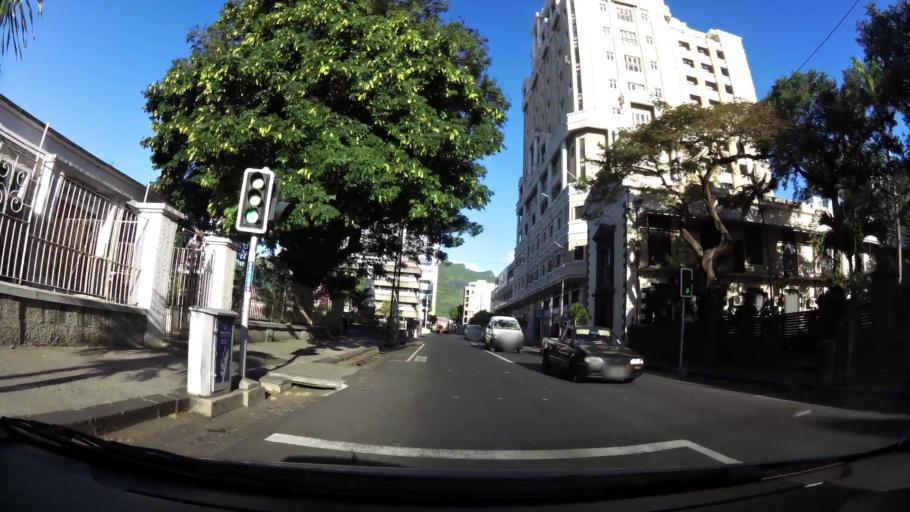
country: MU
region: Port Louis
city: Port Louis
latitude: -20.1648
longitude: 57.5054
